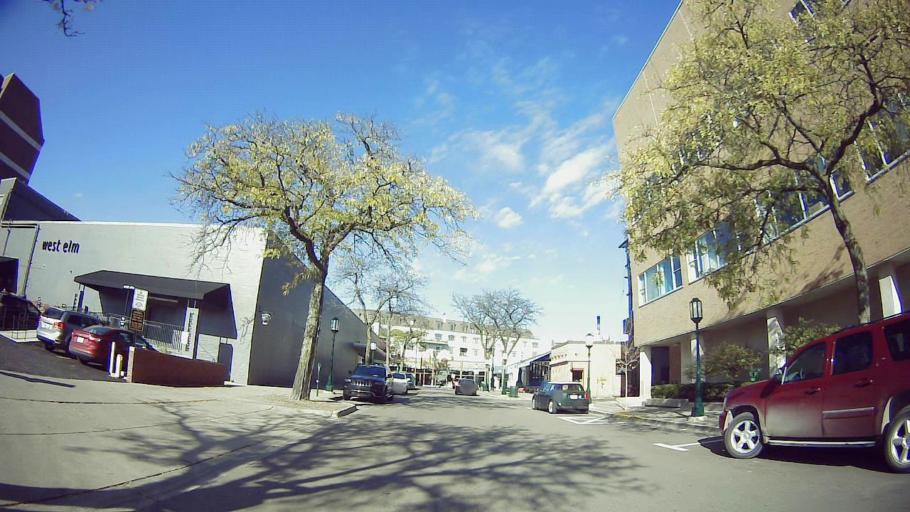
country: US
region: Michigan
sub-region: Oakland County
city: Birmingham
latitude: 42.5466
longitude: -83.2167
